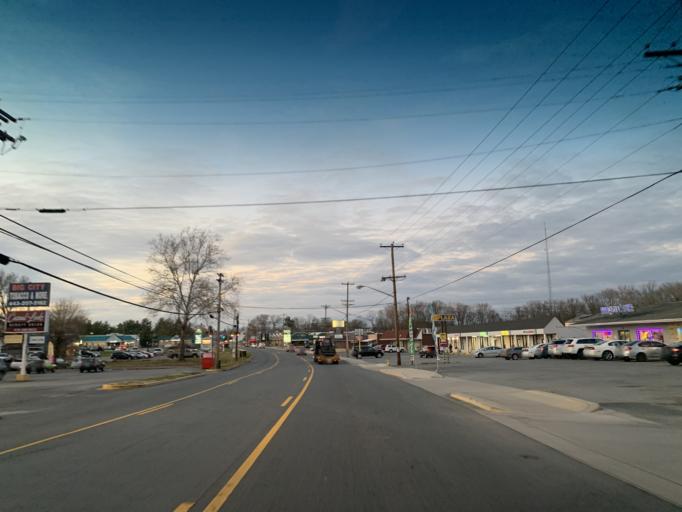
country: US
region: Maryland
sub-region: Cecil County
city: Elkton
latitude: 39.6028
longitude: -75.8291
